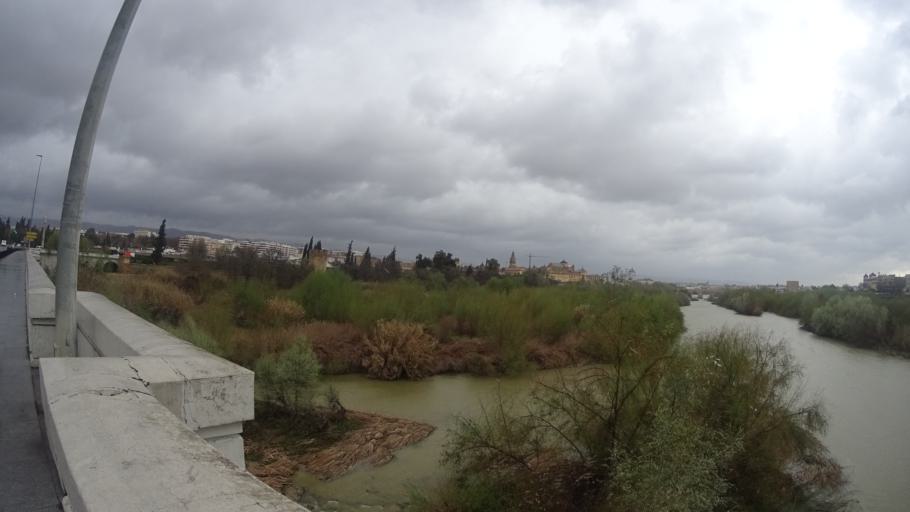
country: ES
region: Andalusia
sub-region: Province of Cordoba
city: Cordoba
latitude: 37.8720
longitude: -4.7822
